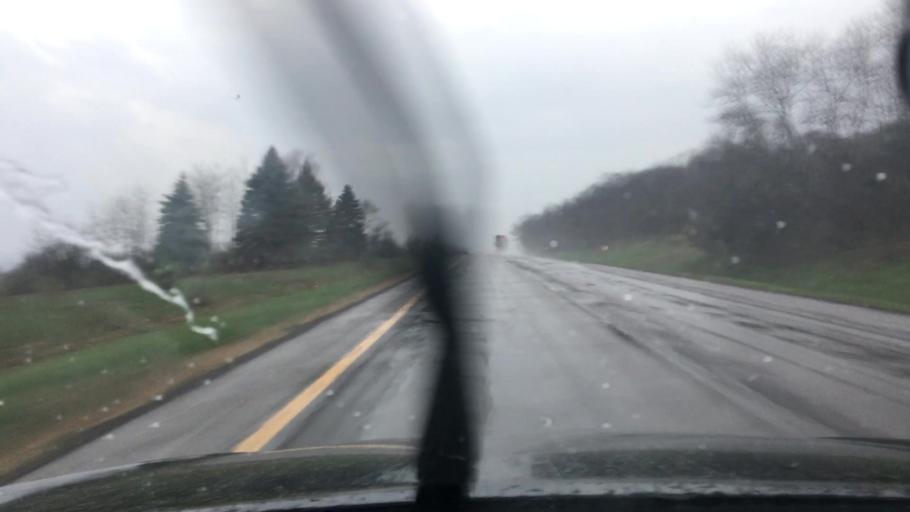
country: US
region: New York
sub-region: Chautauqua County
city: Lakewood
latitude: 42.1427
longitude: -79.3553
